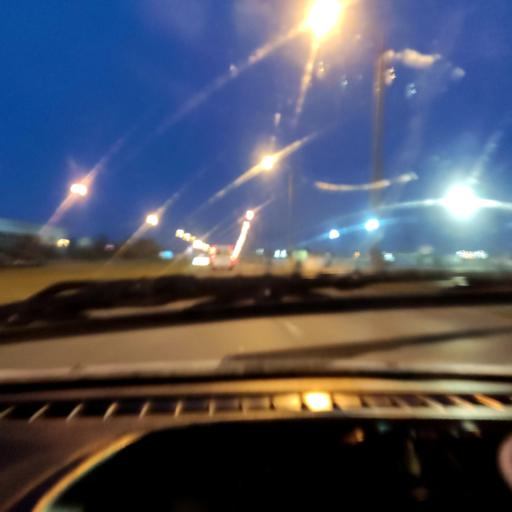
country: RU
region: Samara
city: Tol'yatti
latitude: 53.5563
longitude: 49.3462
